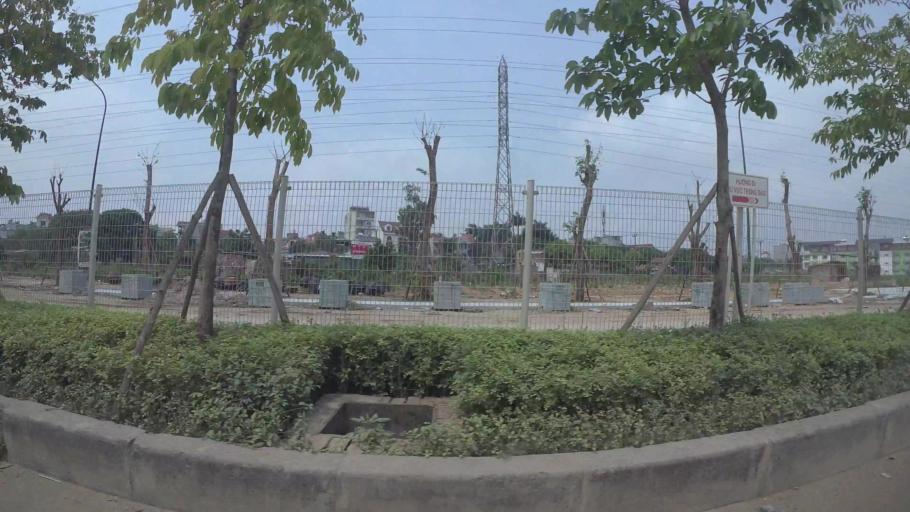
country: VN
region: Ha Noi
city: Tay Ho
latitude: 21.0849
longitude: 105.8053
